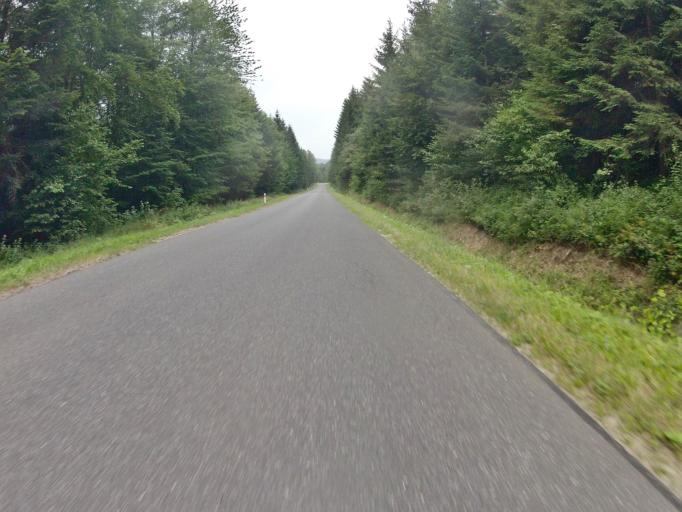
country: PL
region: Subcarpathian Voivodeship
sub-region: Powiat jasielski
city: Krempna
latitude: 49.5379
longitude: 21.5006
